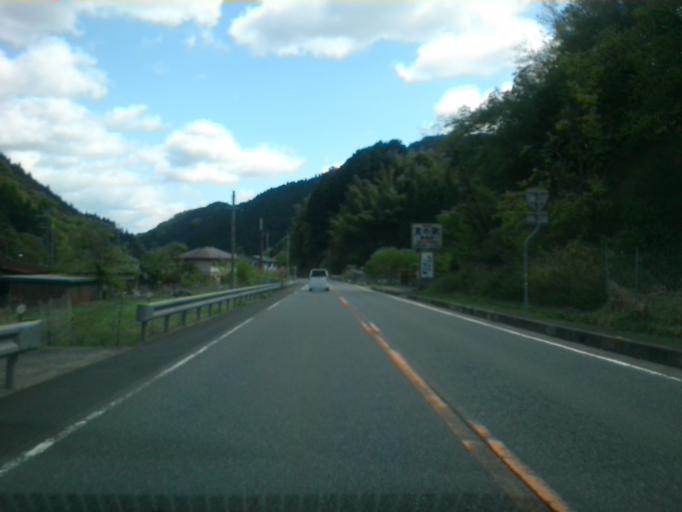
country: JP
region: Kyoto
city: Fukuchiyama
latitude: 35.3609
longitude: 135.0511
